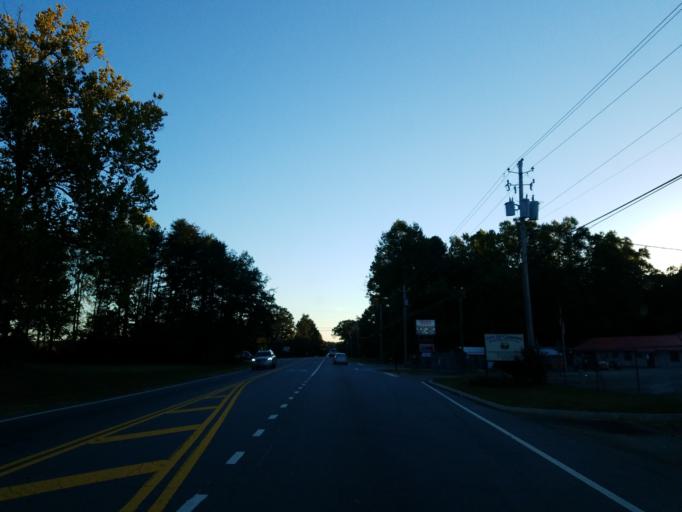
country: US
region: Georgia
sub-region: Forsyth County
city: Cumming
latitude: 34.2468
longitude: -84.1151
